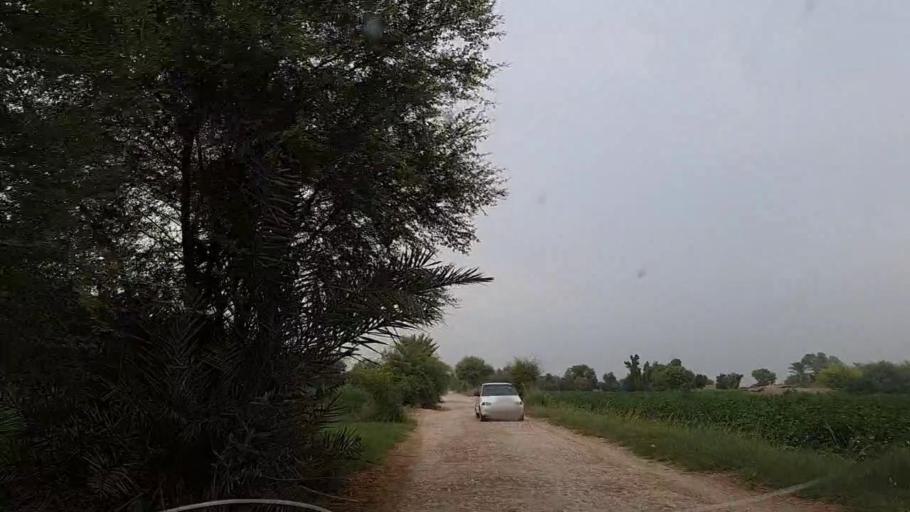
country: PK
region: Sindh
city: Khanpur
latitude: 27.8299
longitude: 69.6111
